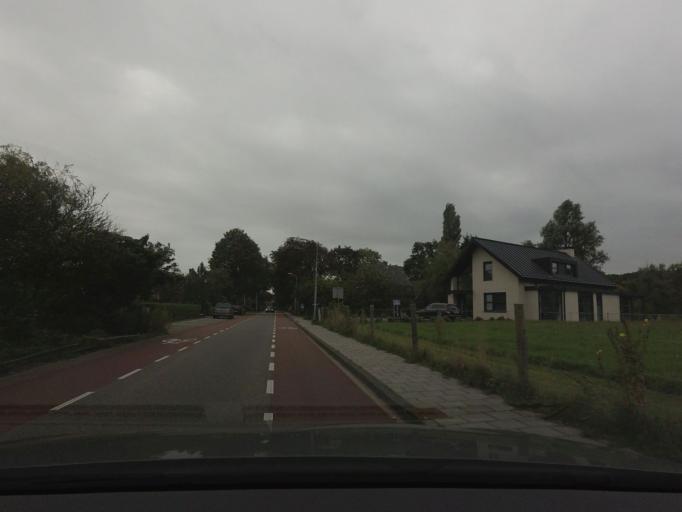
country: NL
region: North Holland
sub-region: Gemeente Schagen
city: Harenkarspel
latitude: 52.7114
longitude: 4.6874
